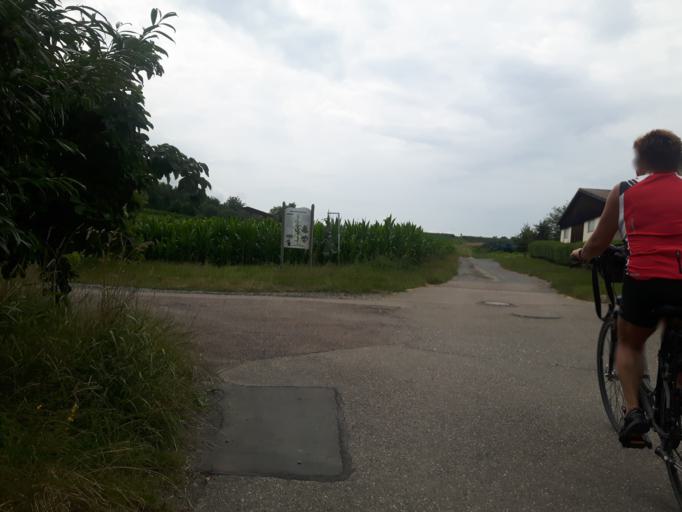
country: DE
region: Baden-Wuerttemberg
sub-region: Regierungsbezirk Stuttgart
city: Brackenheim
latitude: 49.0816
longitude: 9.0579
